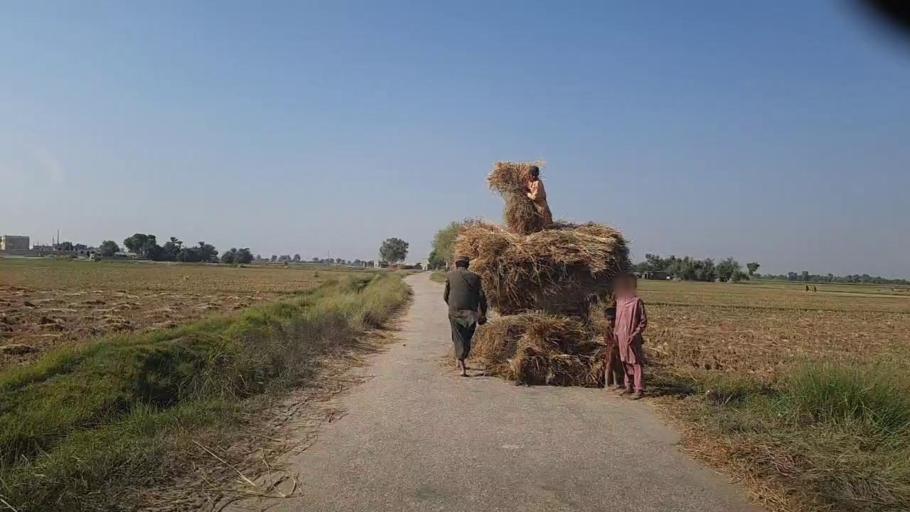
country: PK
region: Sindh
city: Tangwani
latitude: 28.2652
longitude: 68.9313
